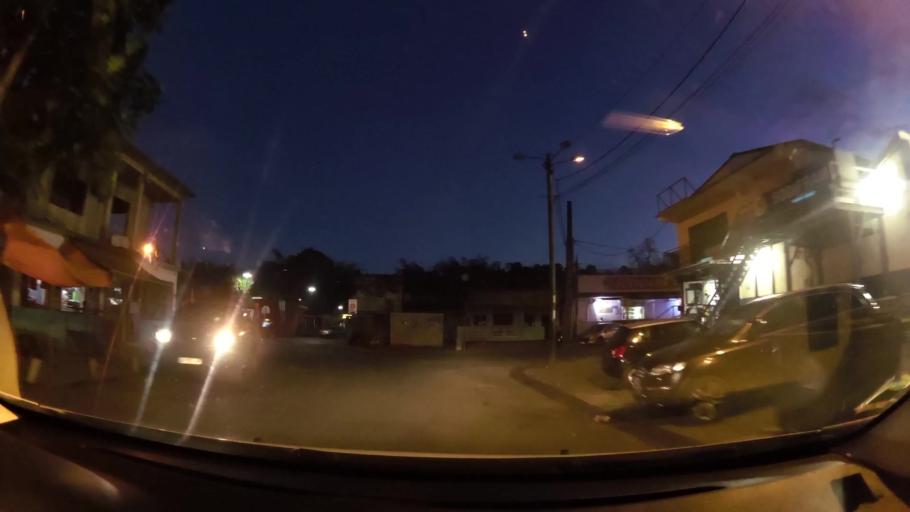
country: YT
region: Bandraboua
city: Bandraboua
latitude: -12.7226
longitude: 45.1204
